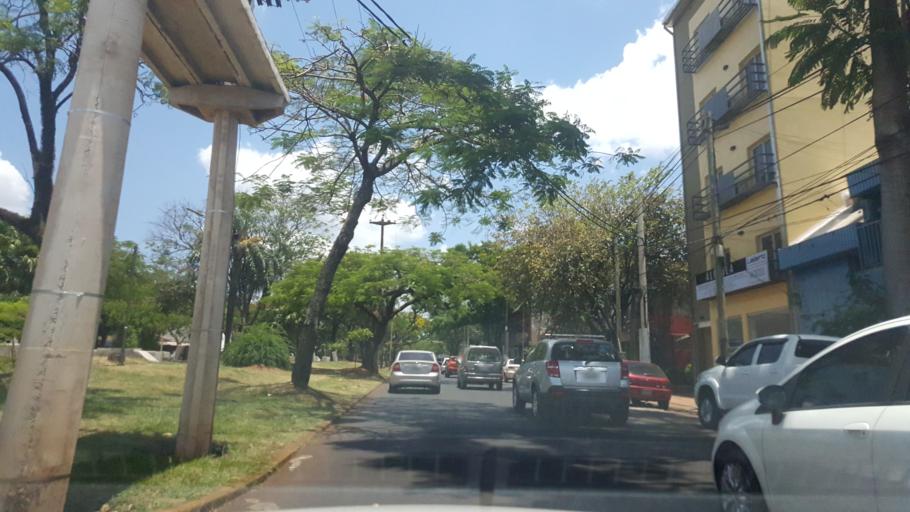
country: AR
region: Misiones
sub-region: Departamento de Capital
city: Posadas
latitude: -27.3689
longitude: -55.9016
